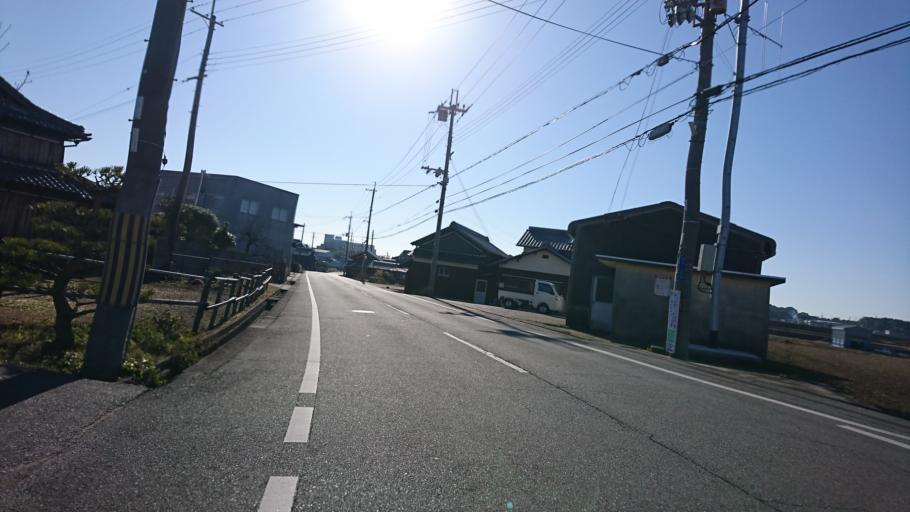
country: JP
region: Hyogo
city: Miki
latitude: 34.7597
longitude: 134.9237
